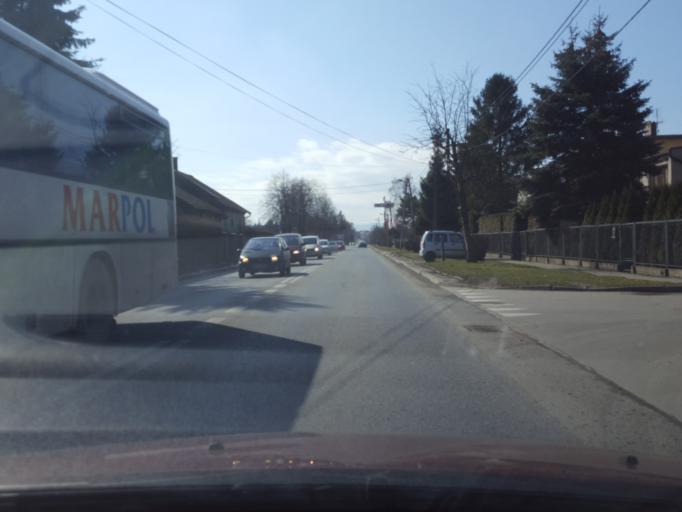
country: PL
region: Lesser Poland Voivodeship
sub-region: Powiat nowosadecki
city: Nowy Sacz
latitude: 49.6382
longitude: 20.6933
